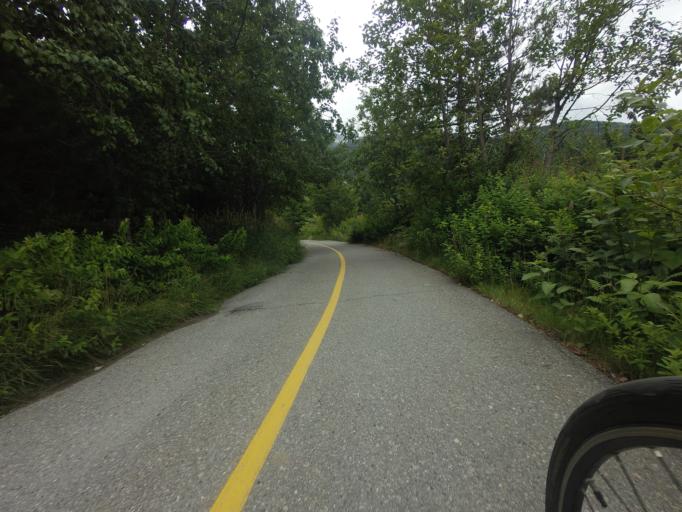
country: CA
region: British Columbia
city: Whistler
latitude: 50.0929
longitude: -122.9996
